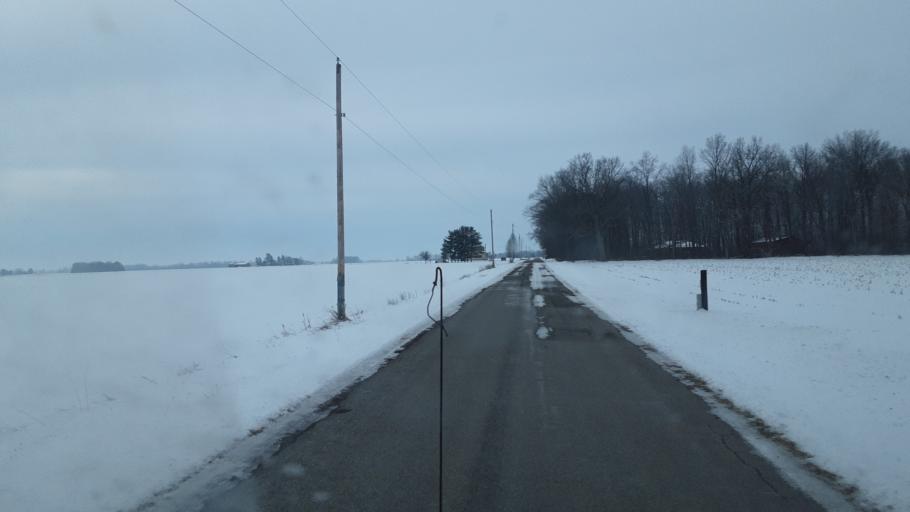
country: US
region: Ohio
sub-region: Union County
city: Marysville
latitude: 40.1415
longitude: -83.4086
